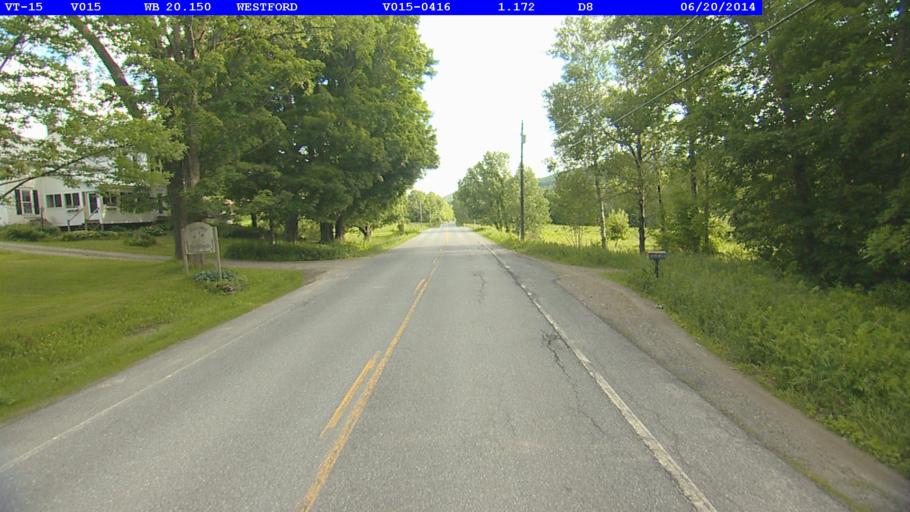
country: US
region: Vermont
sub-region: Chittenden County
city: Jericho
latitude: 44.6104
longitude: -72.9304
